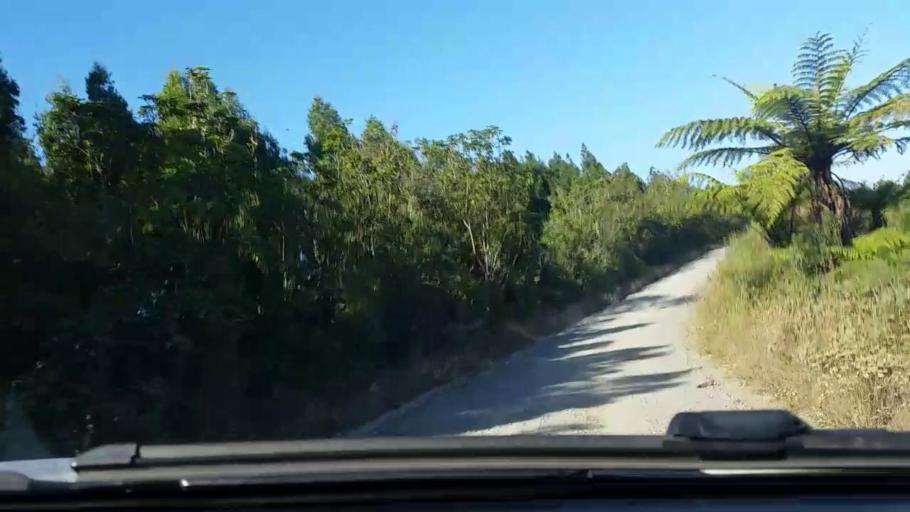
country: NZ
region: Bay of Plenty
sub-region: Kawerau District
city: Kawerau
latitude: -37.9944
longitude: 176.5169
